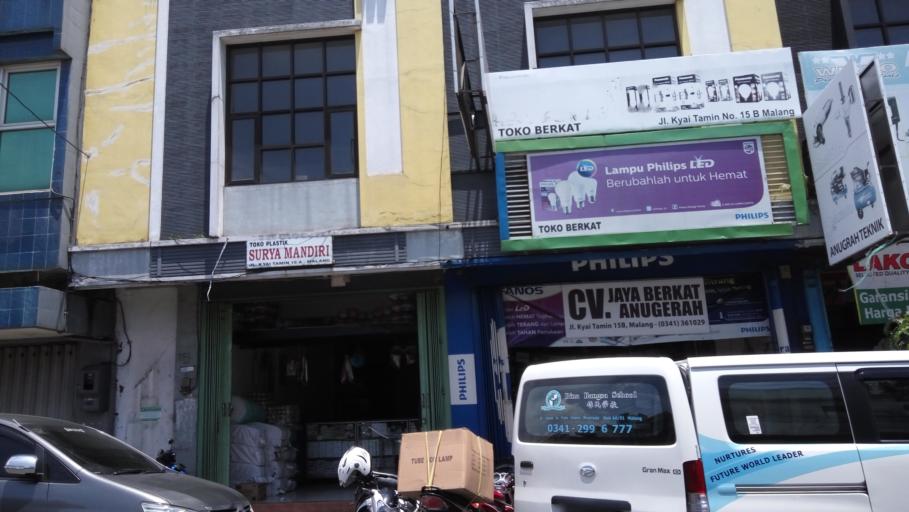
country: ID
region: East Java
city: Malang
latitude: -7.9874
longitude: 112.6311
